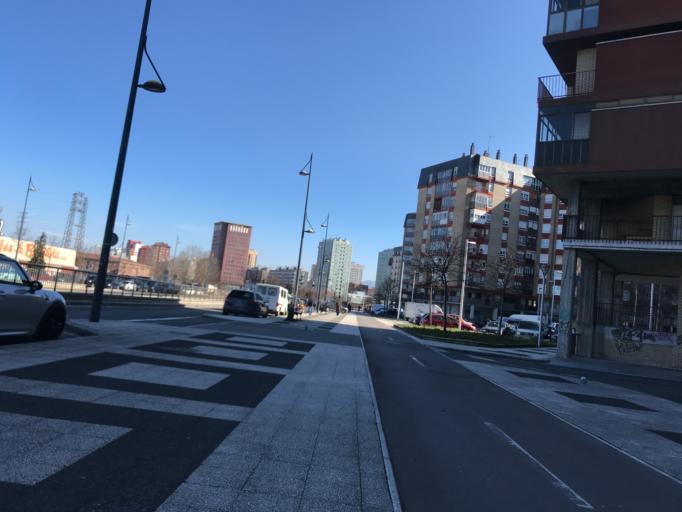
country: ES
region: Basque Country
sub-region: Provincia de Alava
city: Gasteiz / Vitoria
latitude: 42.8577
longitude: -2.6608
